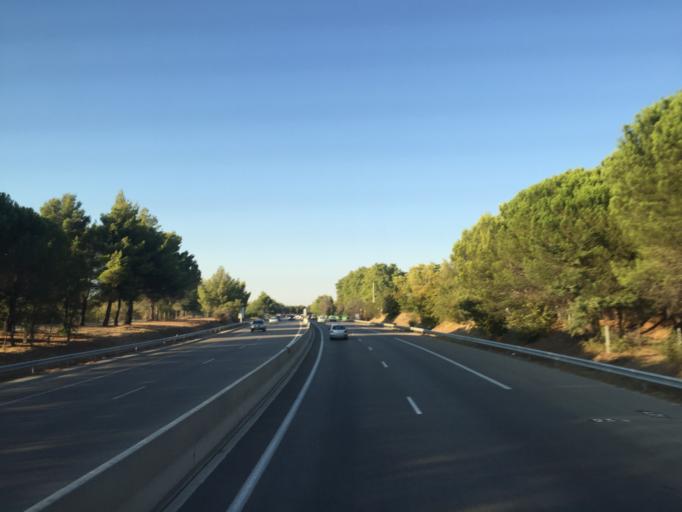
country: FR
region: Provence-Alpes-Cote d'Azur
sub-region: Departement des Bouches-du-Rhone
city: Venelles
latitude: 43.5657
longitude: 5.4641
